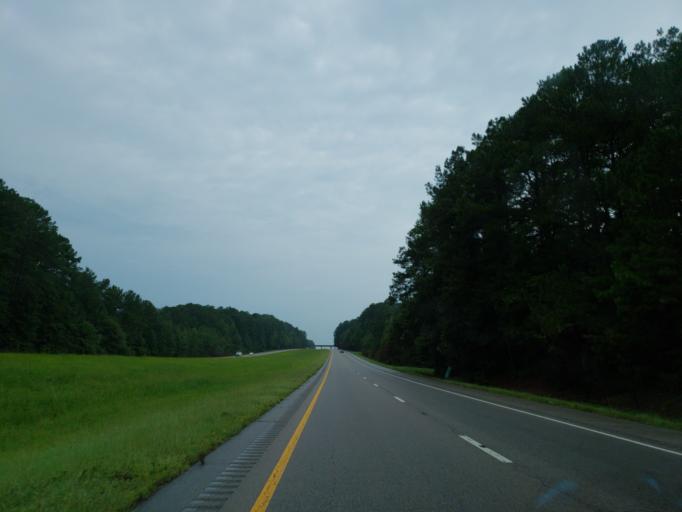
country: US
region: Mississippi
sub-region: Lauderdale County
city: Marion
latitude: 32.4018
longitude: -88.5607
